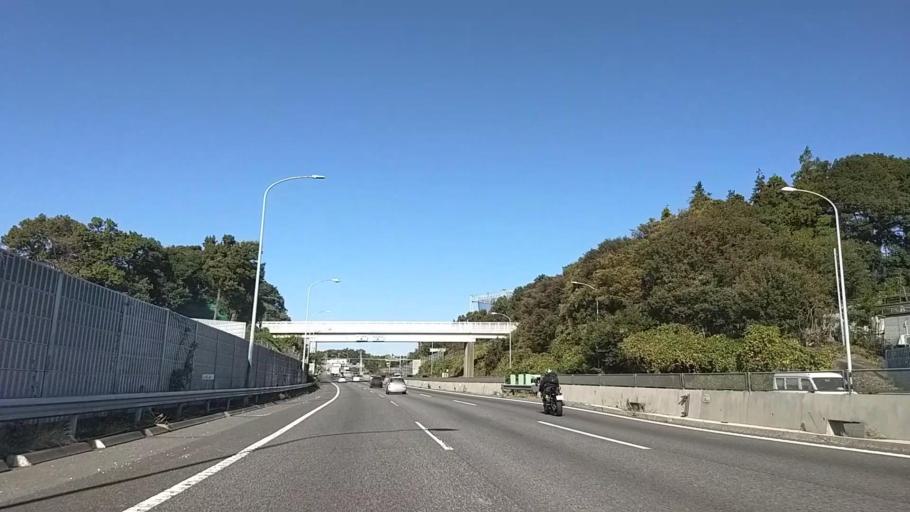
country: JP
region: Kanagawa
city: Minami-rinkan
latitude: 35.4760
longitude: 139.5271
